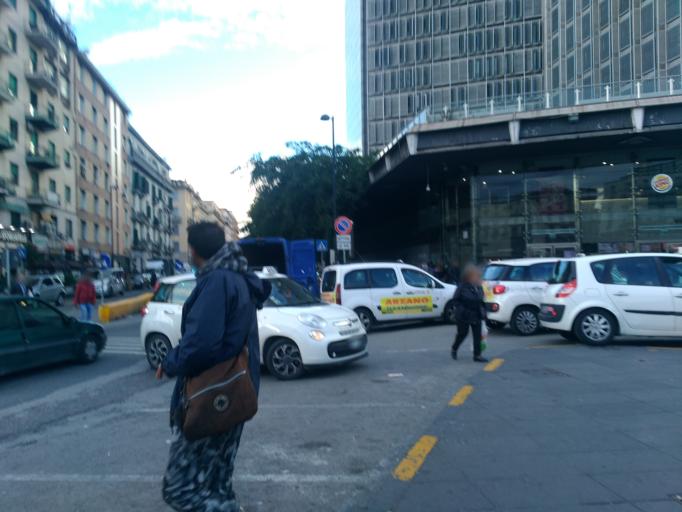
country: IT
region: Campania
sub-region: Provincia di Napoli
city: Napoli
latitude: 40.8531
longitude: 14.2717
